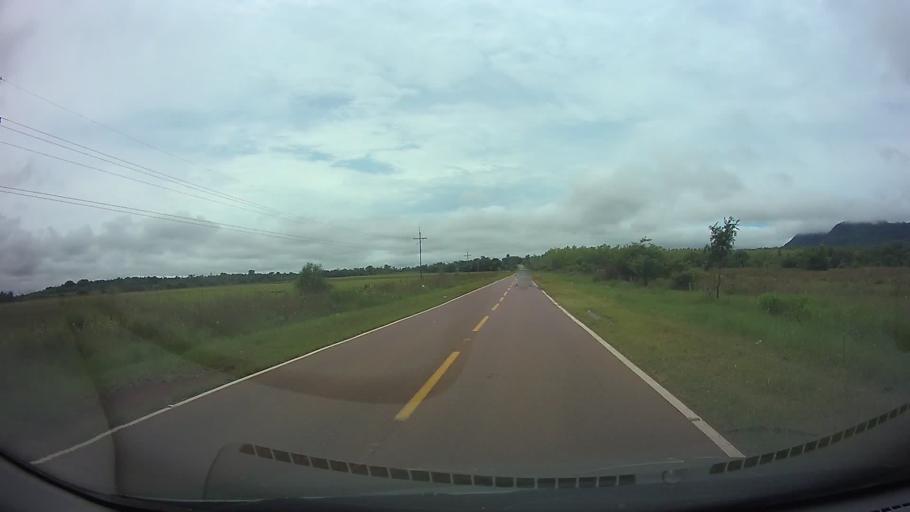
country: PY
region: Paraguari
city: Acahay
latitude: -25.8393
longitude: -57.1495
